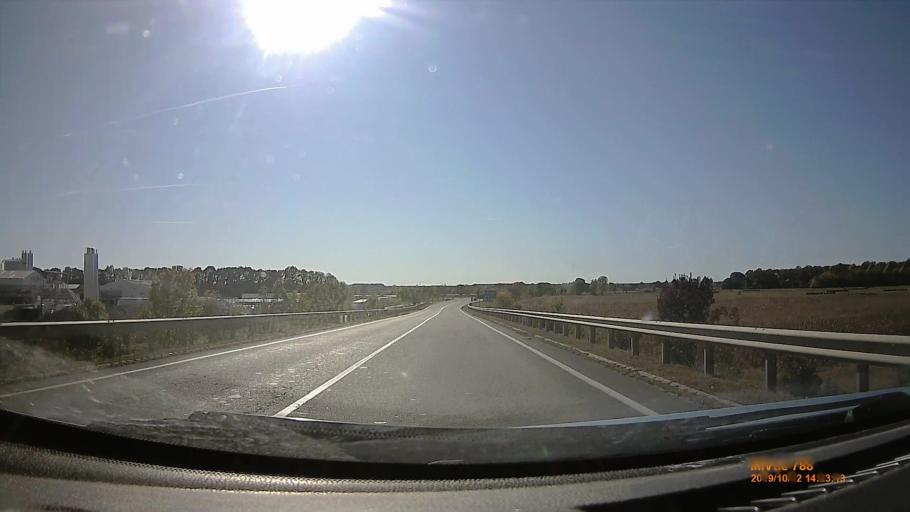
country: HU
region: Hajdu-Bihar
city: Biharkeresztes
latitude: 47.1371
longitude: 21.7035
